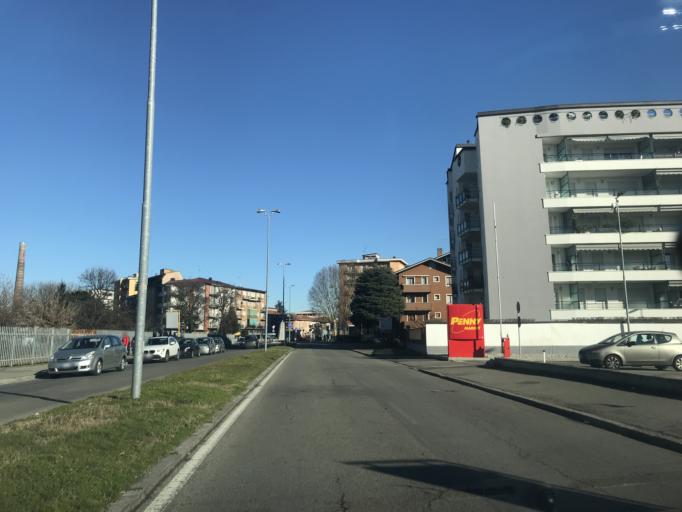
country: IT
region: Lombardy
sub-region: Provincia di Lodi
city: Lodi
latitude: 45.3049
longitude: 9.4975
